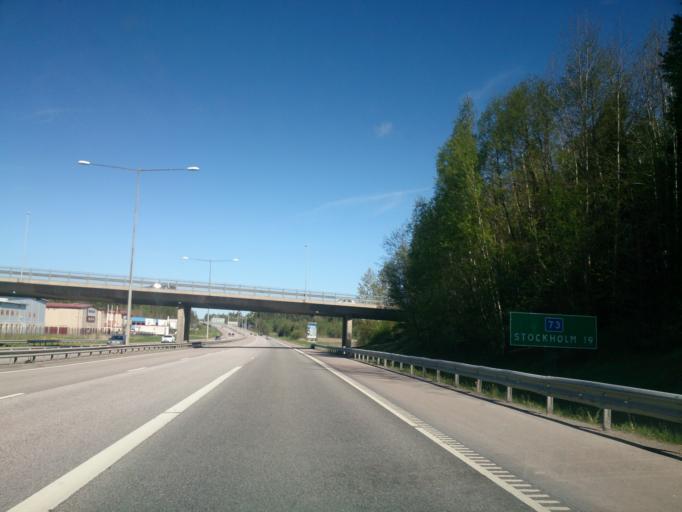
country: SE
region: Stockholm
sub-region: Haninge Kommun
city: Haninge
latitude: 59.1834
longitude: 18.1524
